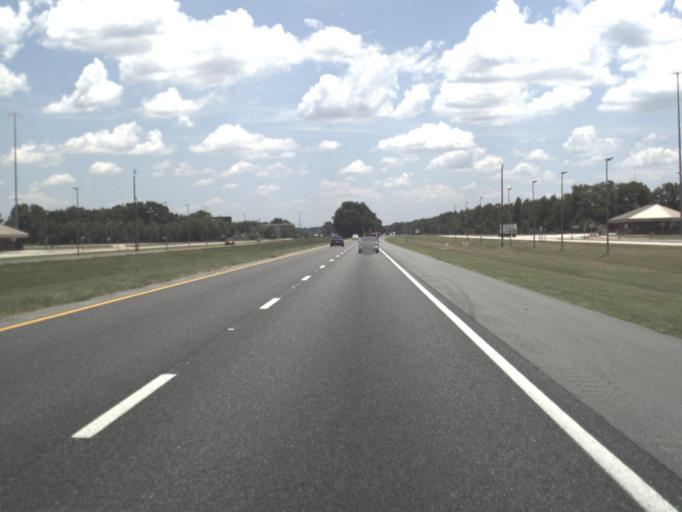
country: US
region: Florida
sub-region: Madison County
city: Madison
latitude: 30.3744
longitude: -83.2745
